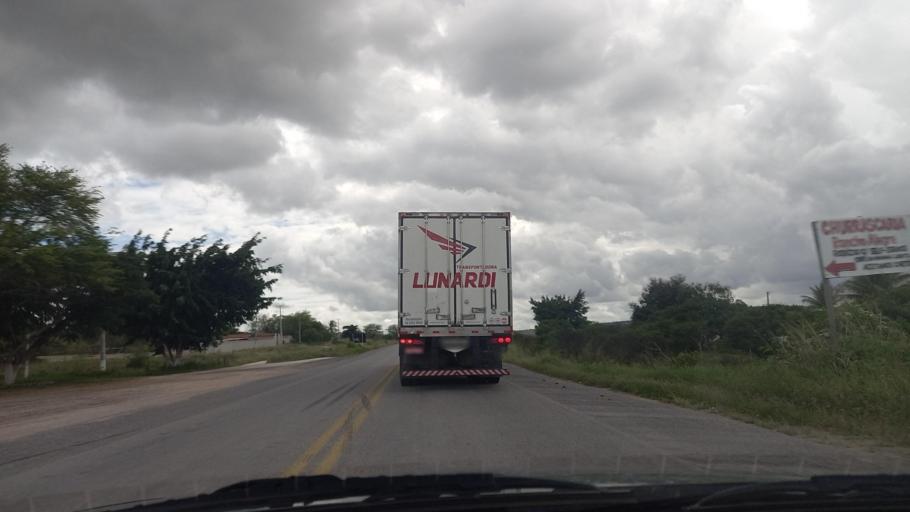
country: BR
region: Pernambuco
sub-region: Lajedo
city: Lajedo
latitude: -8.6670
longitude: -36.3684
